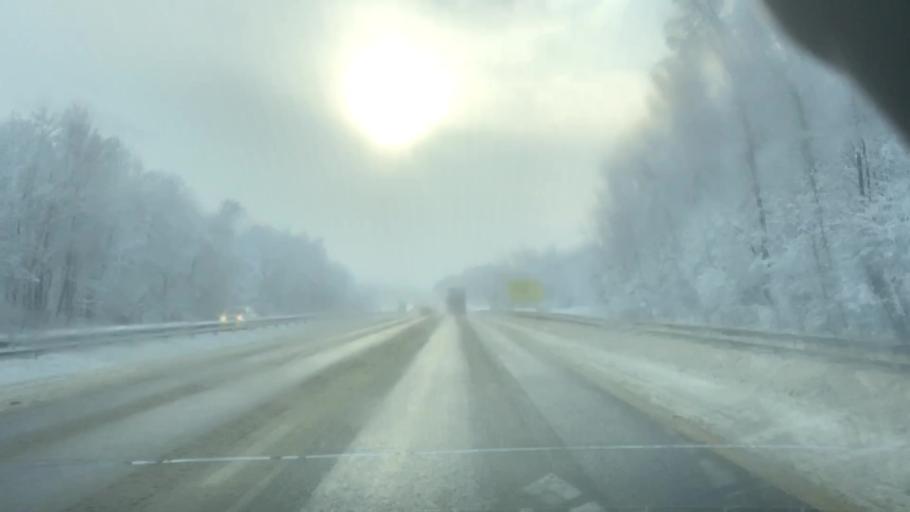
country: RU
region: Tula
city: Venev
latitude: 54.5226
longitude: 38.1686
